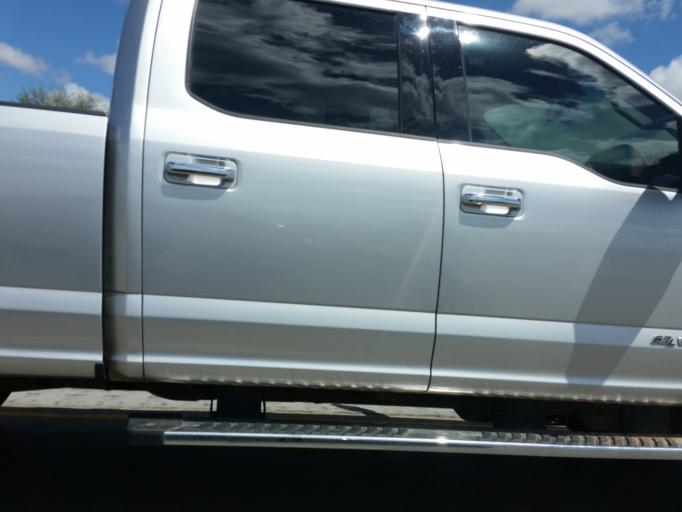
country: US
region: Arkansas
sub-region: Craighead County
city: Bay
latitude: 35.7987
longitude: -90.6208
